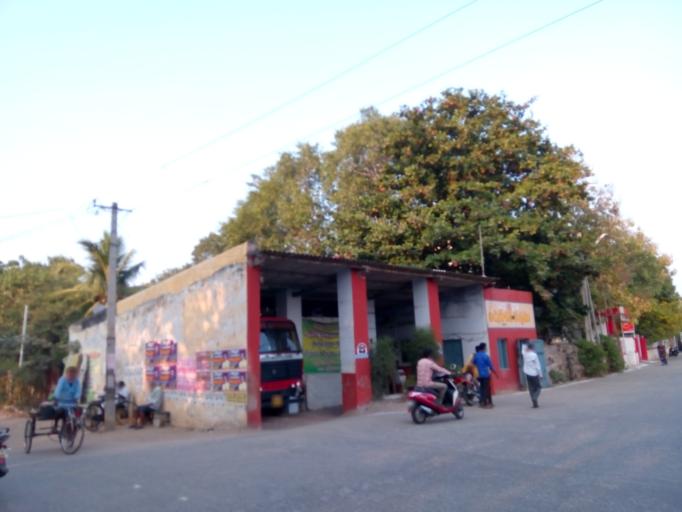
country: IN
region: Andhra Pradesh
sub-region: Prakasam
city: Chirala
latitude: 15.8289
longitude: 80.3514
